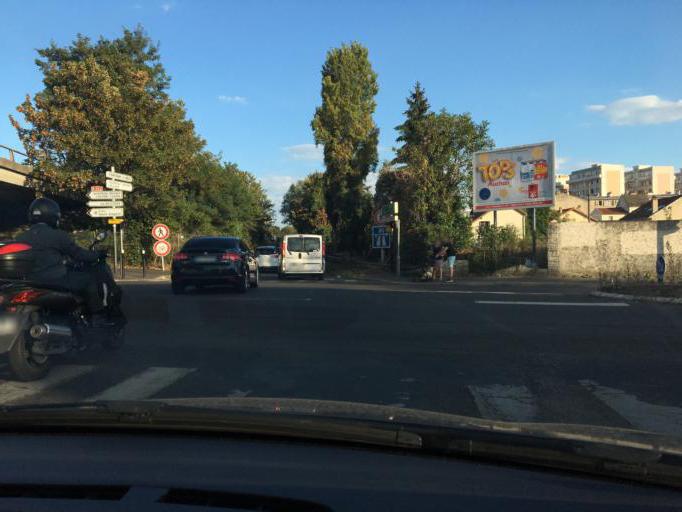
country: FR
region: Ile-de-France
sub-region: Departement de Seine-Saint-Denis
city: Montreuil
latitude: 48.8708
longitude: 2.4510
